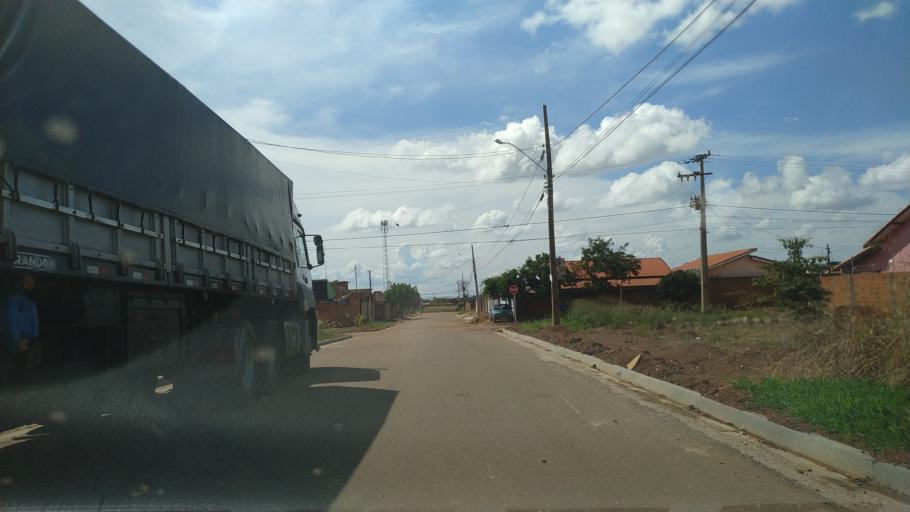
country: BR
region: Mato Grosso
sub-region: Pontes E Lacerda
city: Pontes e Lacerda
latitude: -15.2492
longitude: -59.3156
